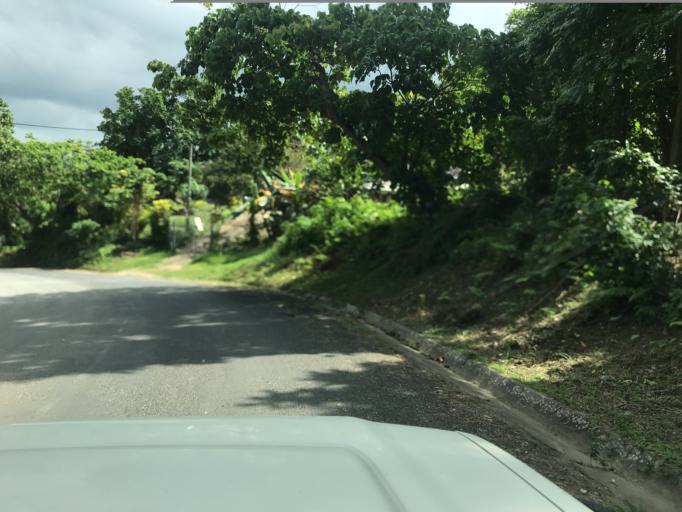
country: VU
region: Sanma
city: Luganville
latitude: -15.5103
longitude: 167.1784
